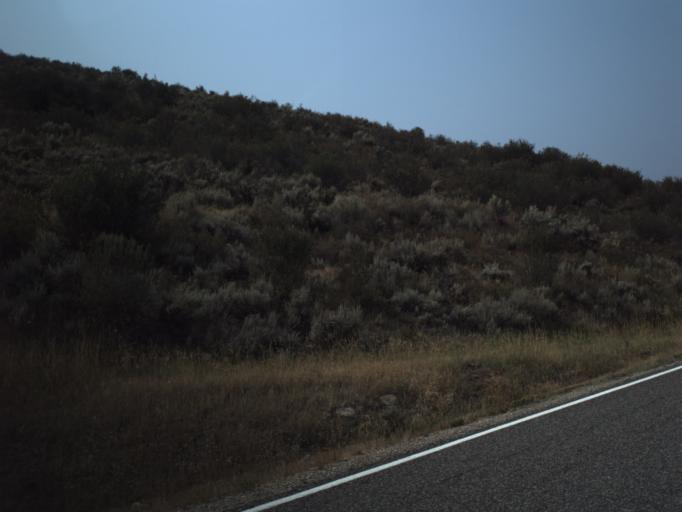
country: US
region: Utah
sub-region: Summit County
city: Coalville
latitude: 40.9863
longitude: -111.5318
